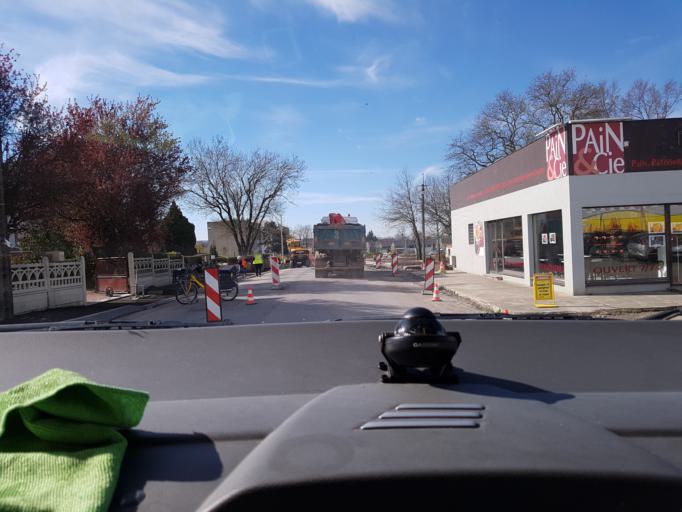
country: FR
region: Bourgogne
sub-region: Departement de Saone-et-Loire
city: Gueugnon
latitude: 46.5954
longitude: 4.0666
